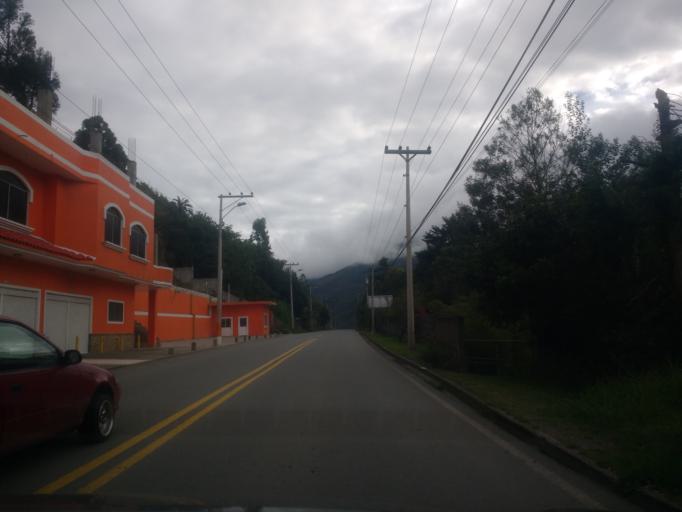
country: EC
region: Azuay
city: La Union
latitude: -2.8491
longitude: -78.7768
